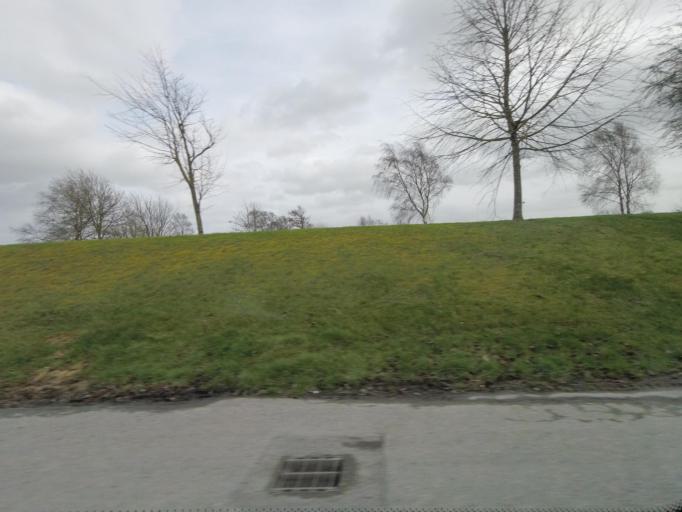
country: IE
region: Leinster
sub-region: Kildare
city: Kilcullen
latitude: 53.1399
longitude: -6.7369
